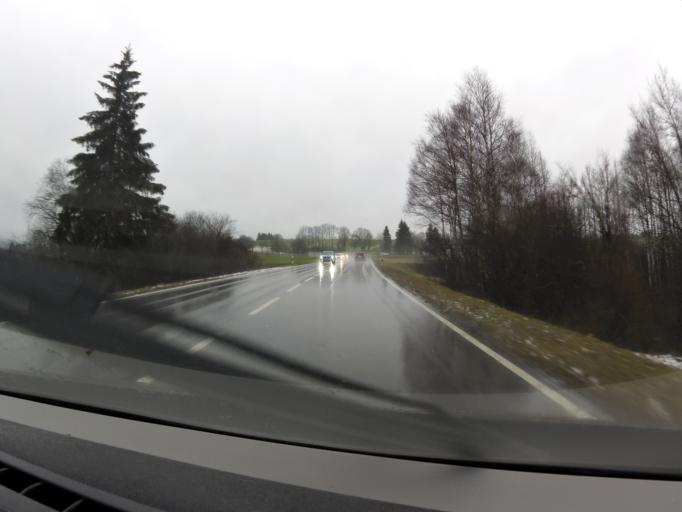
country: DE
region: Bavaria
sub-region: Upper Bavaria
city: Greiling
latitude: 47.7599
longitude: 11.6010
